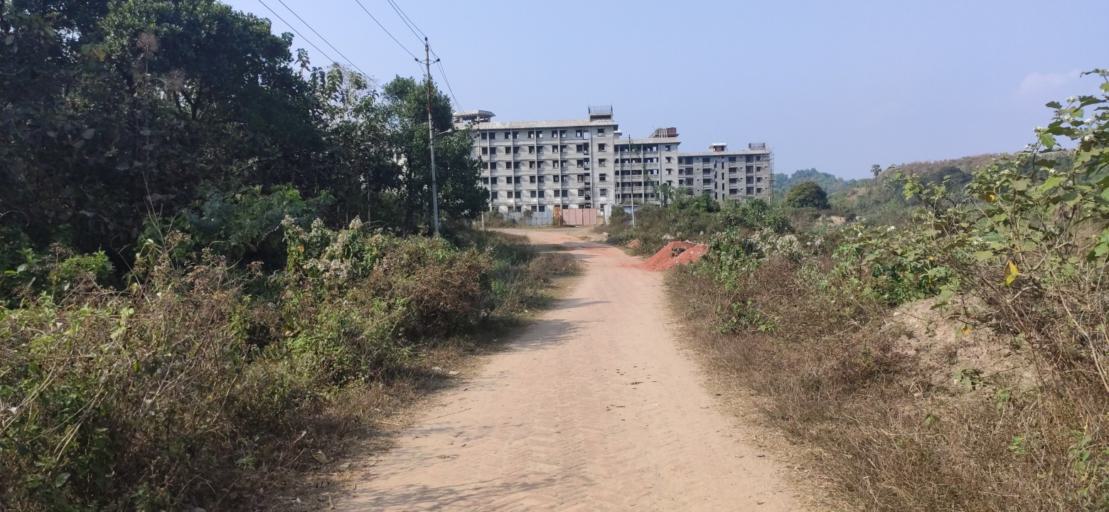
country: BD
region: Chittagong
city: Chittagong
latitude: 22.4756
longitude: 91.7844
